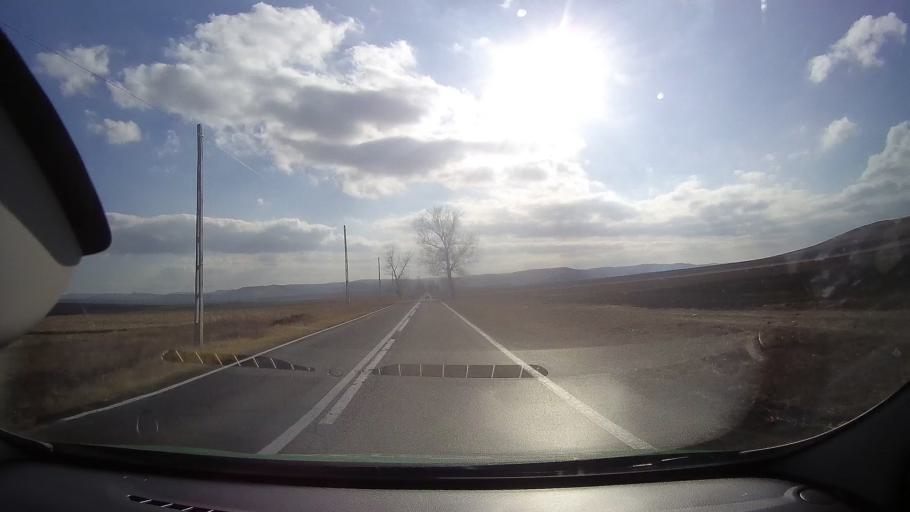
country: RO
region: Tulcea
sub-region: Comuna Nalbant
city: Nicolae Balcescu
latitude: 45.0141
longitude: 28.5997
